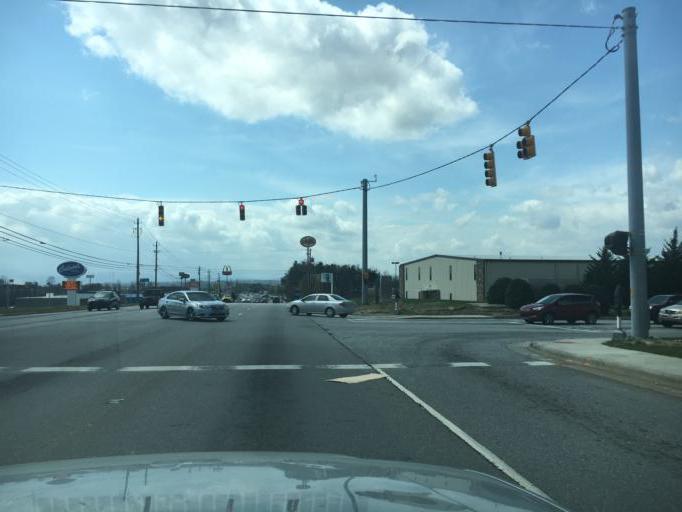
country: US
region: North Carolina
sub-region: Buncombe County
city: Royal Pines
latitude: 35.4473
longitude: -82.5324
